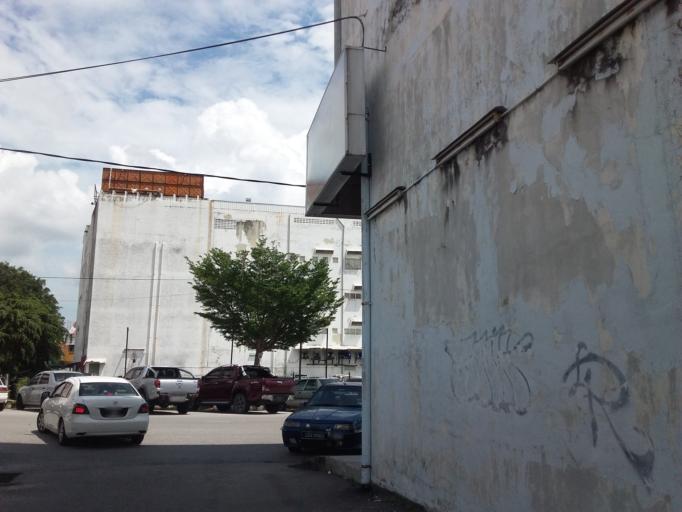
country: MY
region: Johor
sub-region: Daerah Batu Pahat
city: Batu Pahat
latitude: 1.8540
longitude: 102.9272
